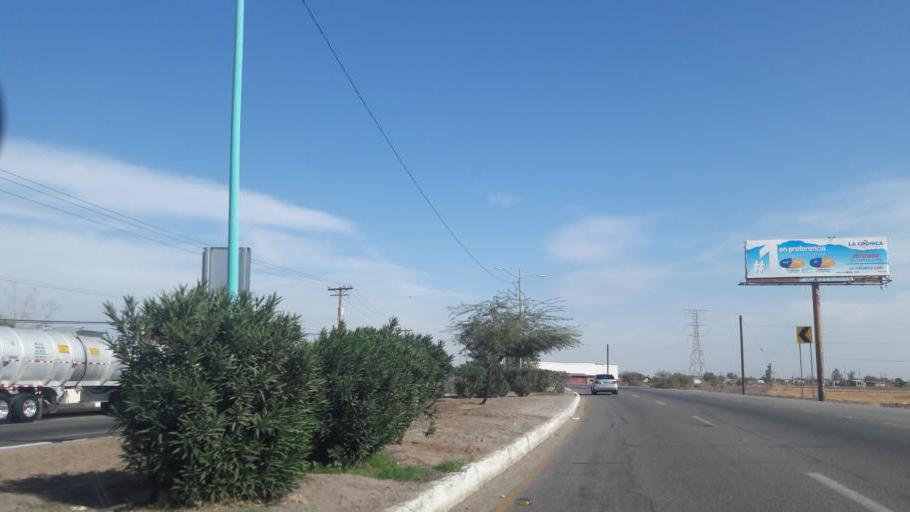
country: MX
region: Baja California
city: Progreso
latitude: 32.5808
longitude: -115.5793
